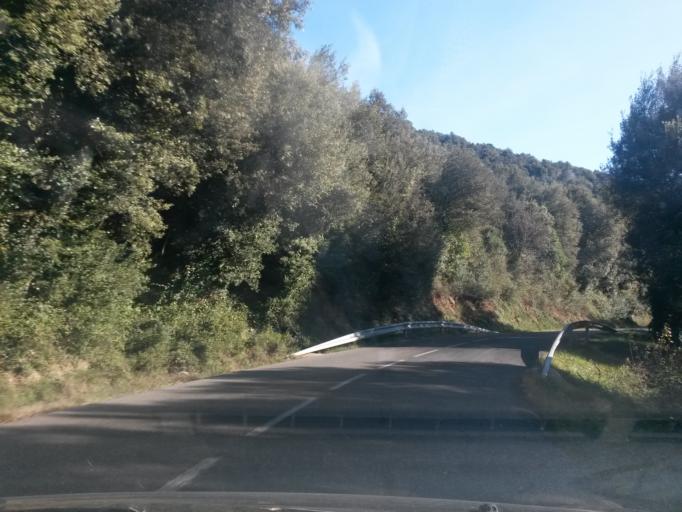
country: ES
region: Catalonia
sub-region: Provincia de Girona
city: Sant Gregori
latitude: 42.0228
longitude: 2.6857
